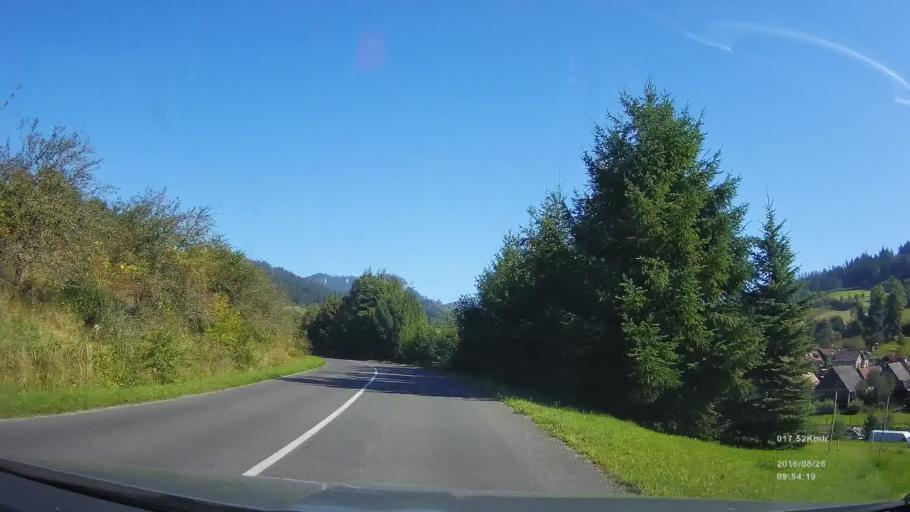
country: SK
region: Zilinsky
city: Ruzomberok
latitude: 49.1139
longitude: 19.4458
